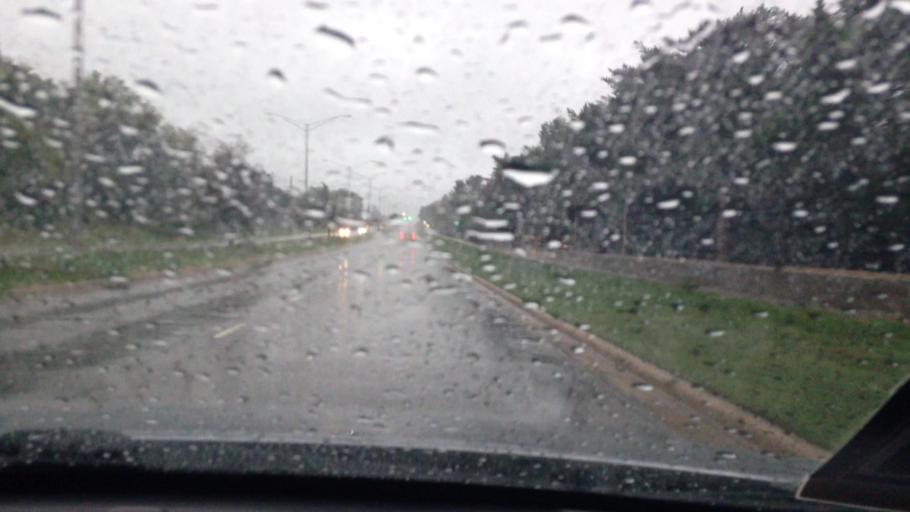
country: US
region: Kansas
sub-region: Johnson County
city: Lenexa
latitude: 38.9077
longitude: -94.7238
